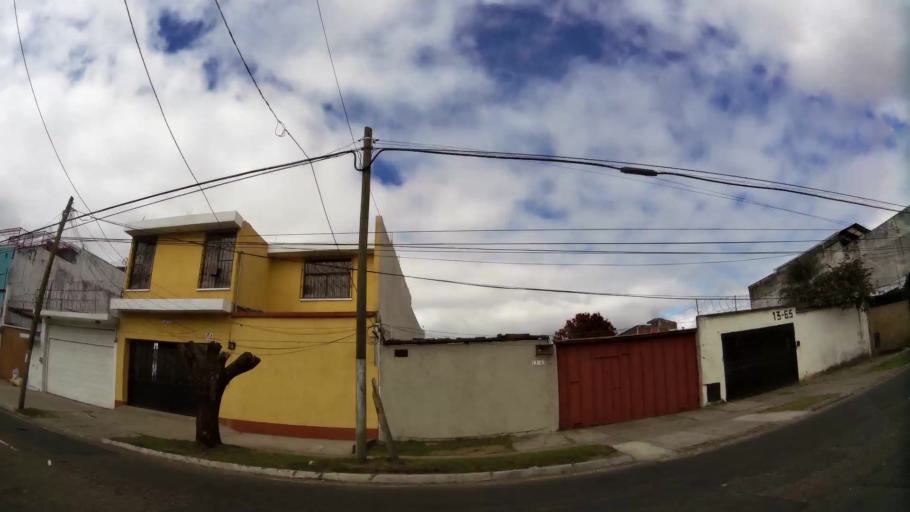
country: GT
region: Guatemala
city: Guatemala City
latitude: 14.6364
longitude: -90.5471
